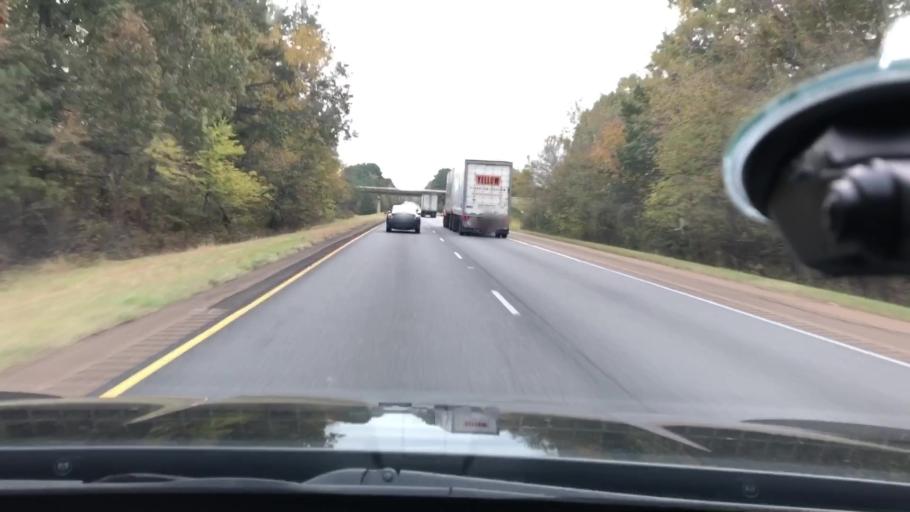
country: US
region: Arkansas
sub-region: Nevada County
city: Prescott
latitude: 33.8475
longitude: -93.3745
